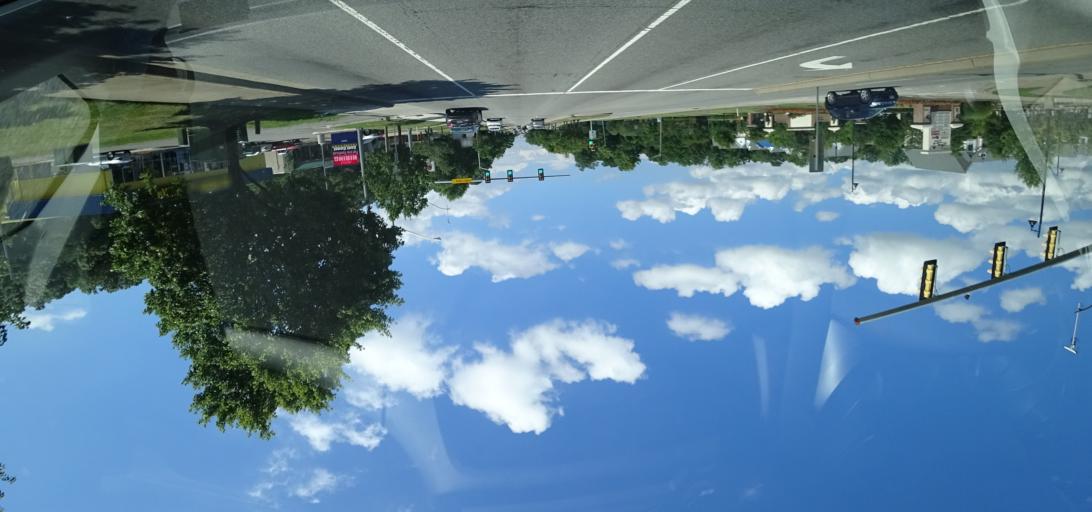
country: US
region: Virginia
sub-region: York County
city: Yorktown
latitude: 37.1421
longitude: -76.5229
